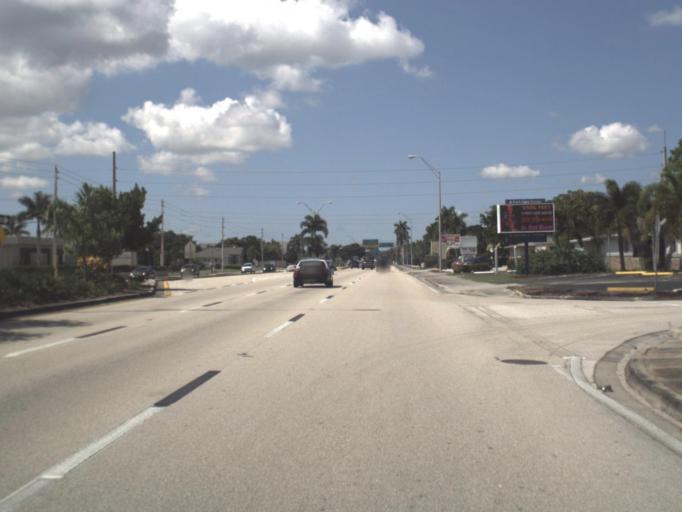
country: US
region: Florida
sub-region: Lee County
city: Pine Manor
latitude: 26.5970
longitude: -81.8782
